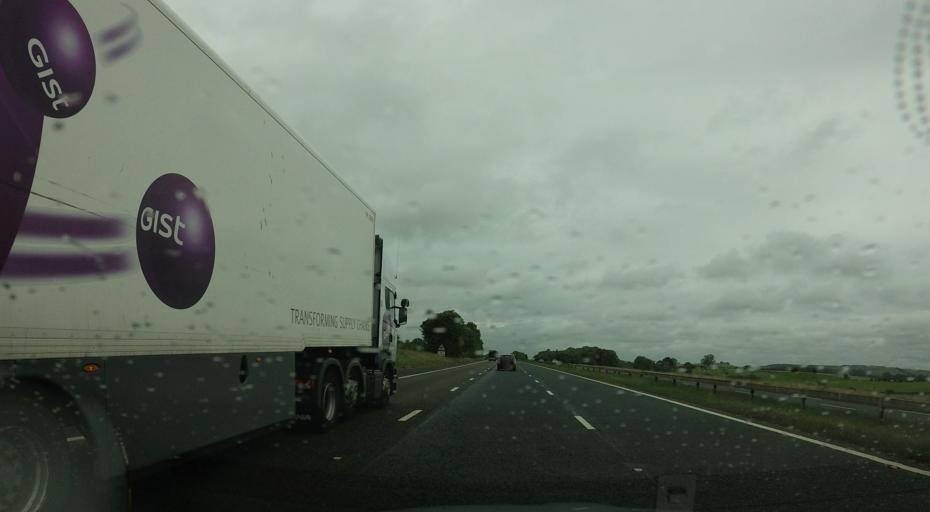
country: GB
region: England
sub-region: Cumbria
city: Penrith
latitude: 54.7380
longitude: -2.8068
